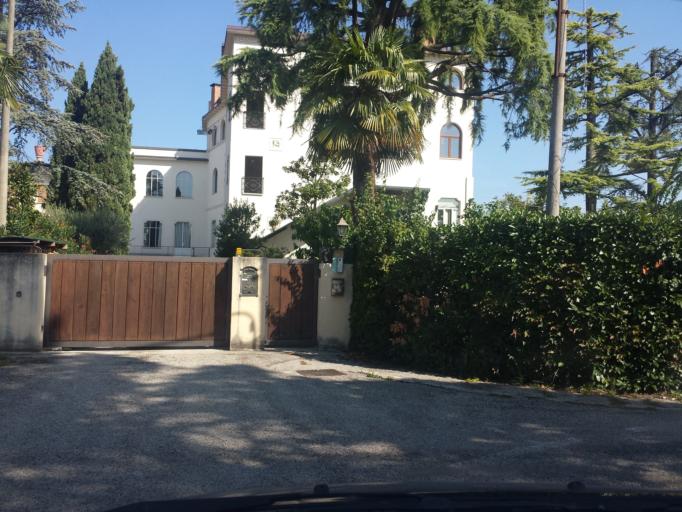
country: IT
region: Veneto
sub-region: Provincia di Vicenza
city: Sandrigo
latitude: 45.6660
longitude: 11.5956
